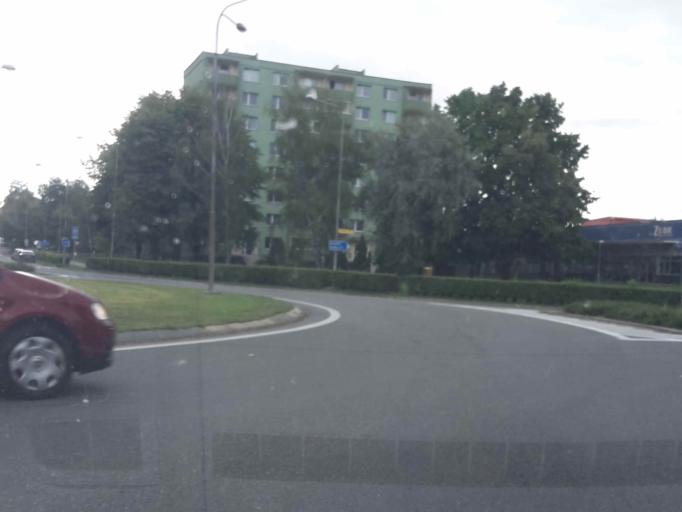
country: CZ
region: Olomoucky
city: Prerov
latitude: 49.4513
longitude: 17.4624
